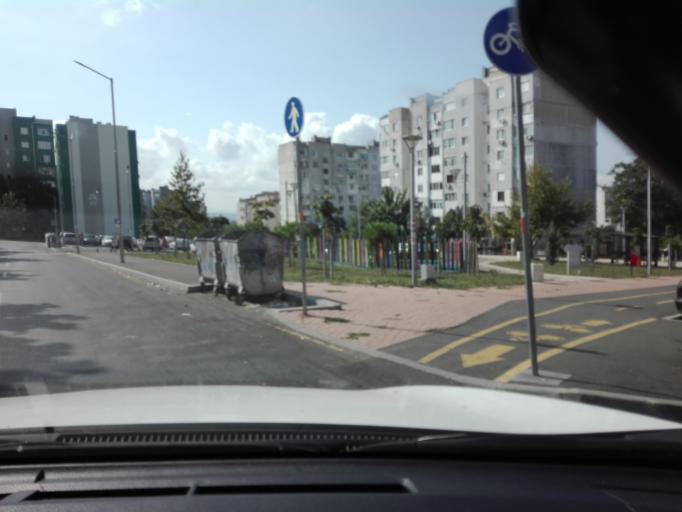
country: BG
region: Burgas
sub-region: Obshtina Burgas
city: Burgas
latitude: 42.4572
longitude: 27.4189
